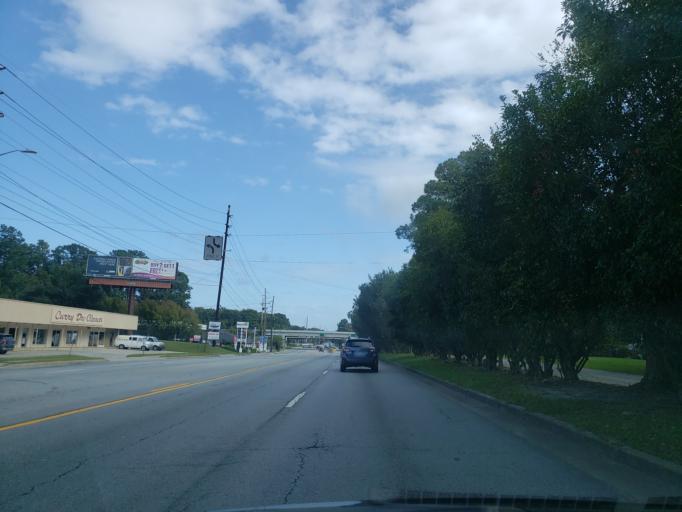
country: US
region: Georgia
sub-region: Chatham County
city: Thunderbolt
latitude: 32.0236
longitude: -81.0917
